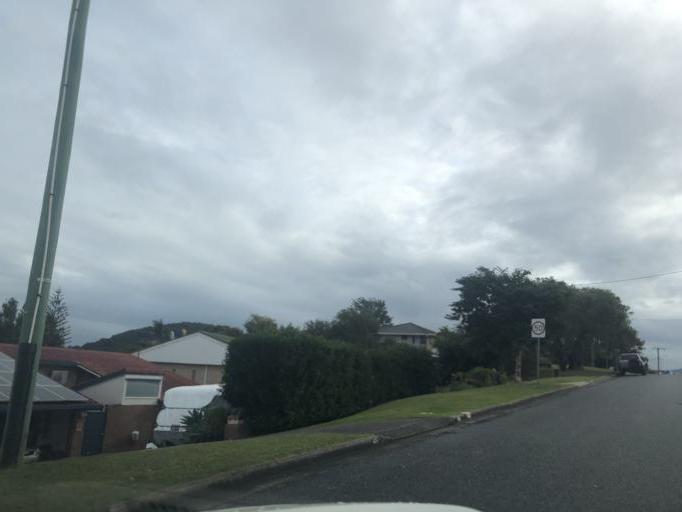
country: AU
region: New South Wales
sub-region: Coffs Harbour
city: Coffs Harbour
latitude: -30.2892
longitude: 153.1118
